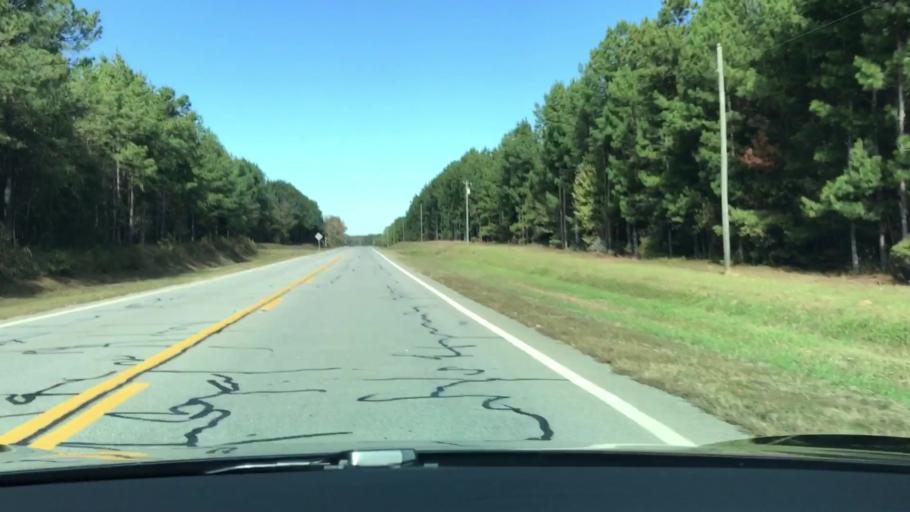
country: US
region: Georgia
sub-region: Glascock County
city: Gibson
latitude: 33.3355
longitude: -82.5691
